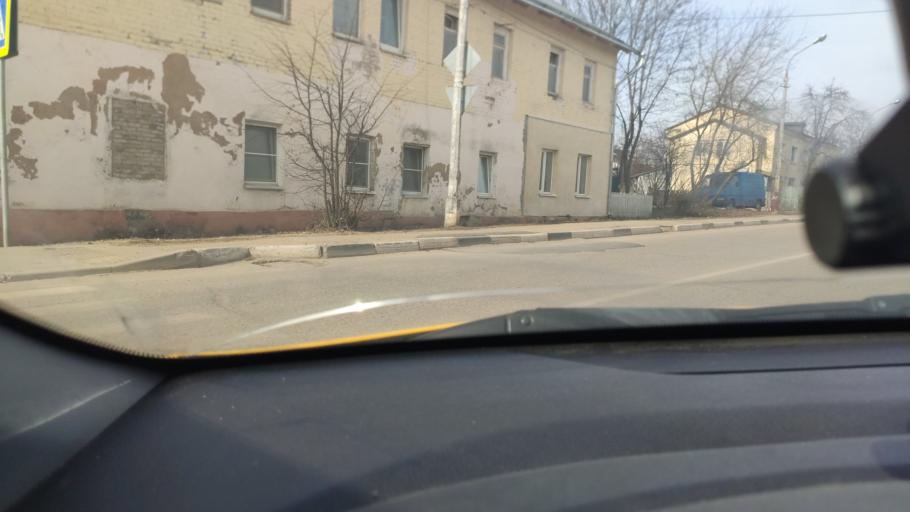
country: RU
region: Moskovskaya
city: Ruza
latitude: 55.7016
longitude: 36.1910
